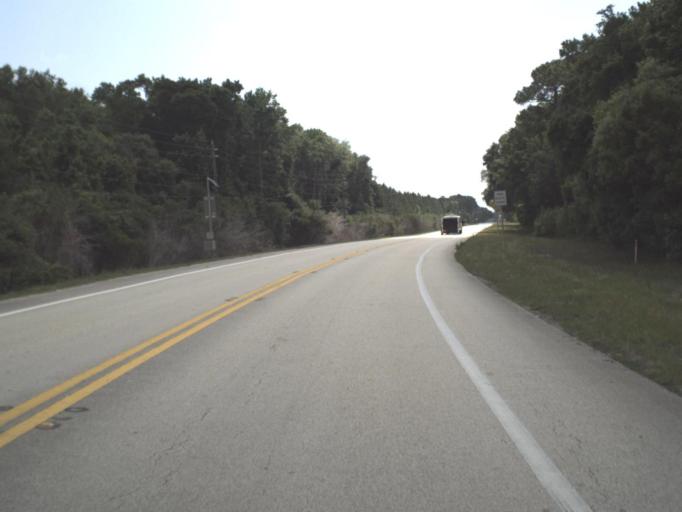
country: US
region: Florida
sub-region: Saint Johns County
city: Saint Augustine Shores
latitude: 29.7562
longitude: -81.3262
